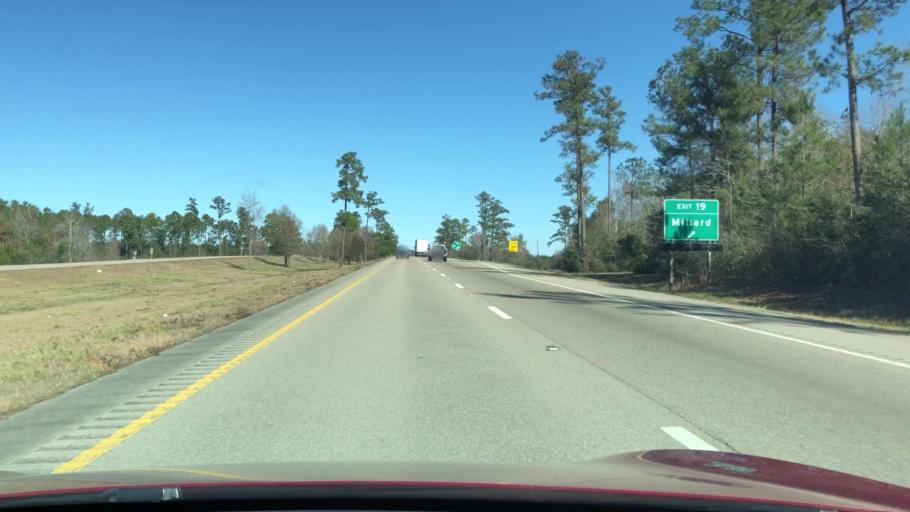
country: US
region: Mississippi
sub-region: Pearl River County
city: Poplarville
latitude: 30.7145
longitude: -89.5560
